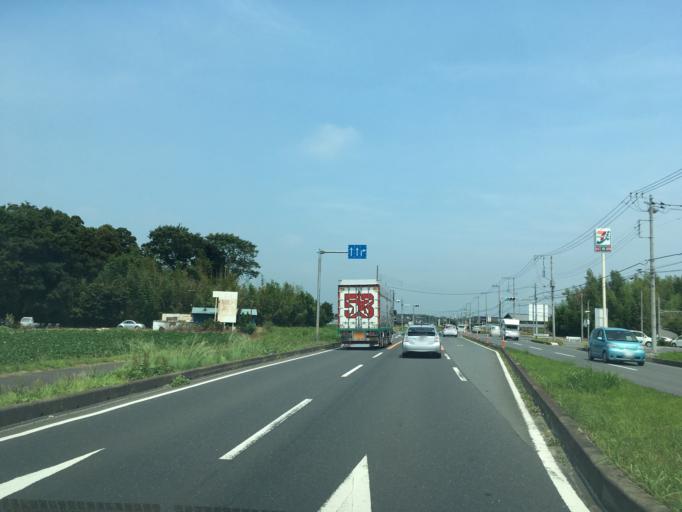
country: JP
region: Ibaraki
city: Hitachi-Naka
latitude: 36.3869
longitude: 140.5784
